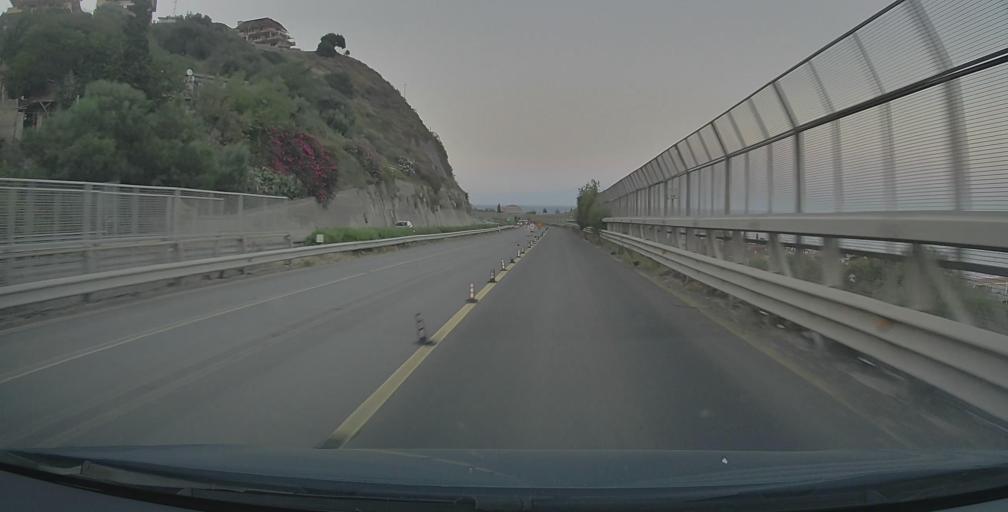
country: IT
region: Sicily
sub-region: Messina
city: Letojanni
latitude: 37.8883
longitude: 15.3145
